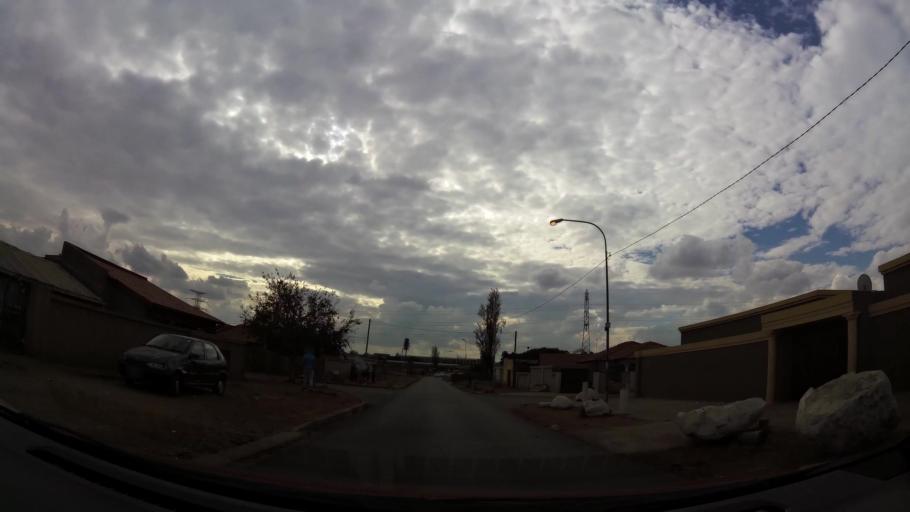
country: ZA
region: Gauteng
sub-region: City of Johannesburg Metropolitan Municipality
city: Soweto
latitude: -26.2426
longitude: 27.8498
